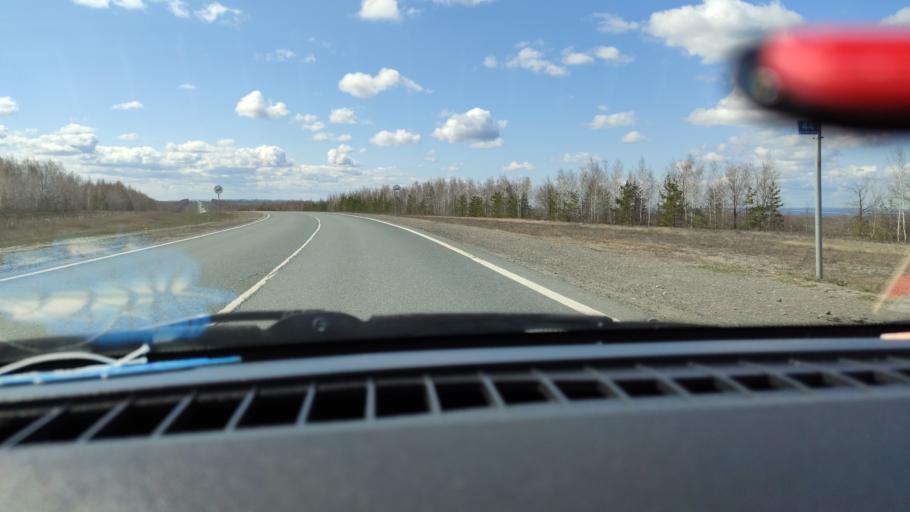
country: RU
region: Saratov
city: Dukhovnitskoye
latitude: 52.8302
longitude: 48.2388
